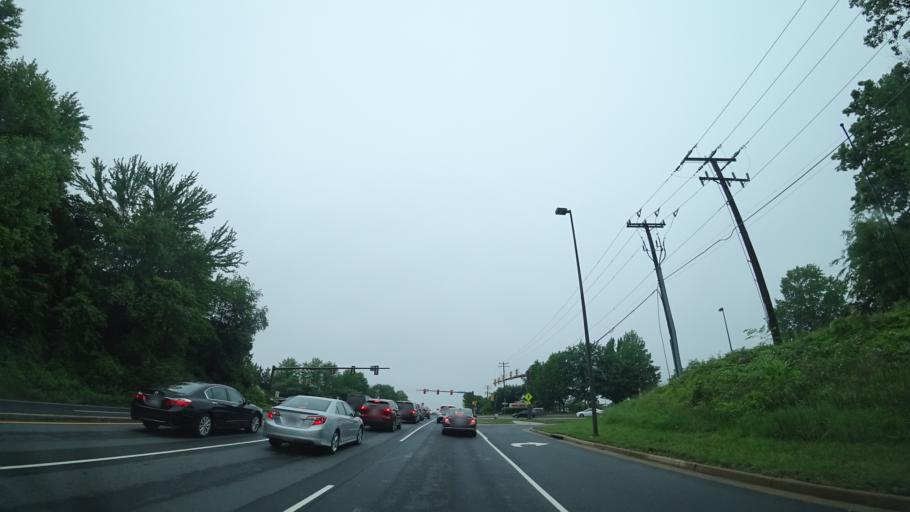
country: US
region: Virginia
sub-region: Fairfax County
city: Reston
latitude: 38.9674
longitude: -77.3530
